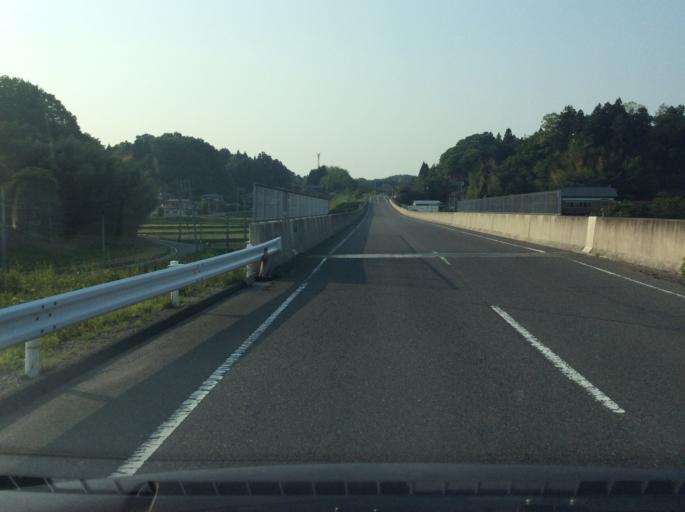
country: JP
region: Fukushima
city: Ishikawa
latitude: 37.2050
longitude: 140.4384
